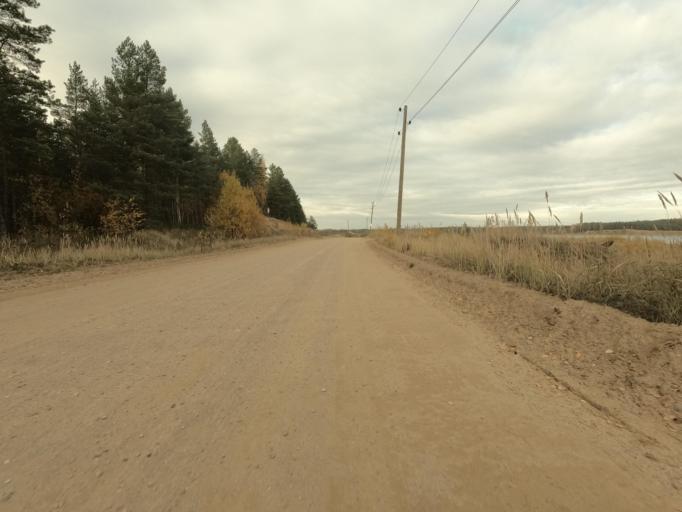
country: RU
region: Leningrad
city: Priladozhskiy
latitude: 59.6982
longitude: 31.3621
